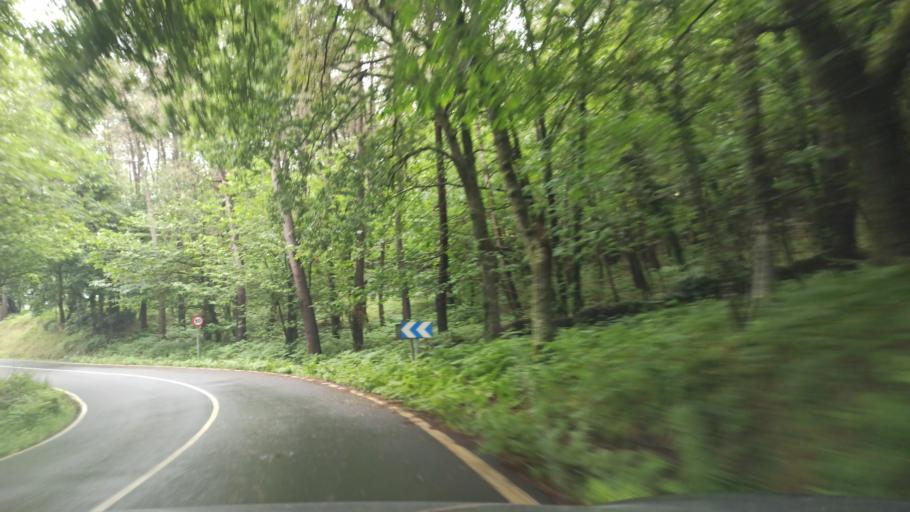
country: ES
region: Galicia
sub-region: Provincia da Coruna
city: Santiso
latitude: 42.7840
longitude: -8.0800
